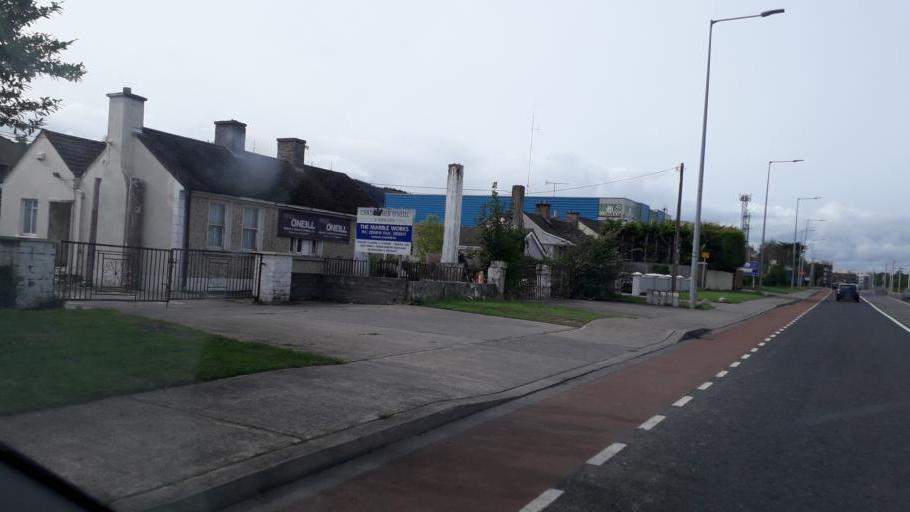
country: IE
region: Leinster
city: Foxrock
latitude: 53.2563
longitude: -6.1909
